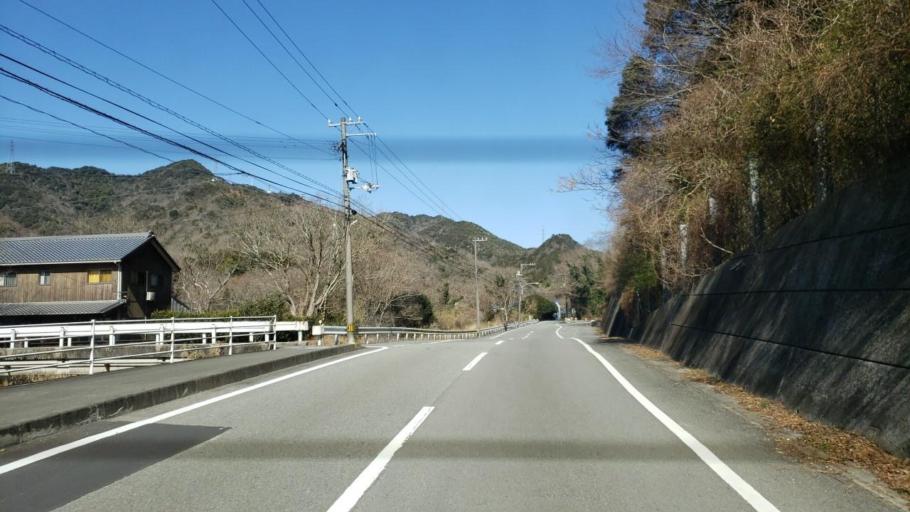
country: JP
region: Tokushima
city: Narutocho-mitsuishi
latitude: 34.1705
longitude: 134.5411
